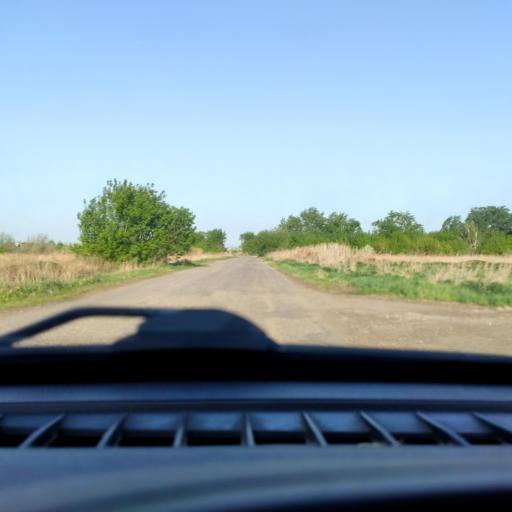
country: RU
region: Samara
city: Tol'yatti
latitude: 53.6483
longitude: 49.3158
